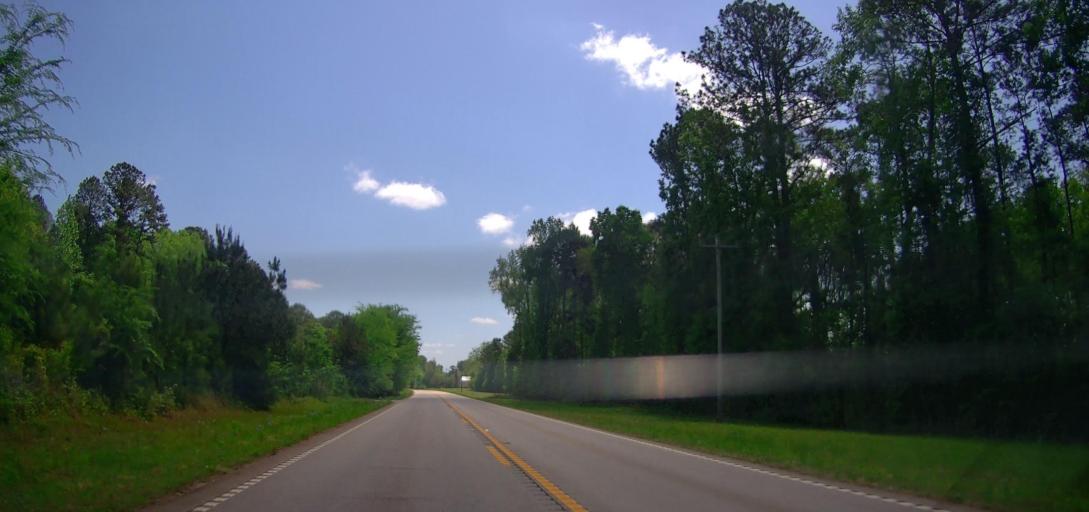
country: US
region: Georgia
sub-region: Jasper County
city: Monticello
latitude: 33.1914
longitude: -83.6506
